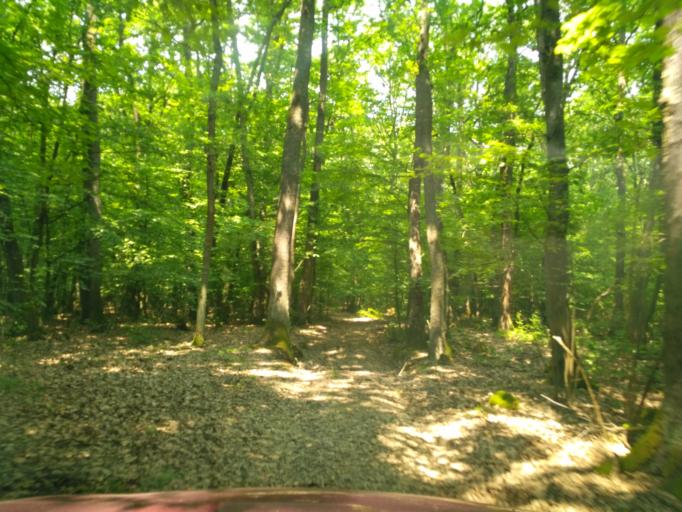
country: SK
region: Kosicky
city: Moldava nad Bodvou
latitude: 48.6490
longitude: 21.0352
